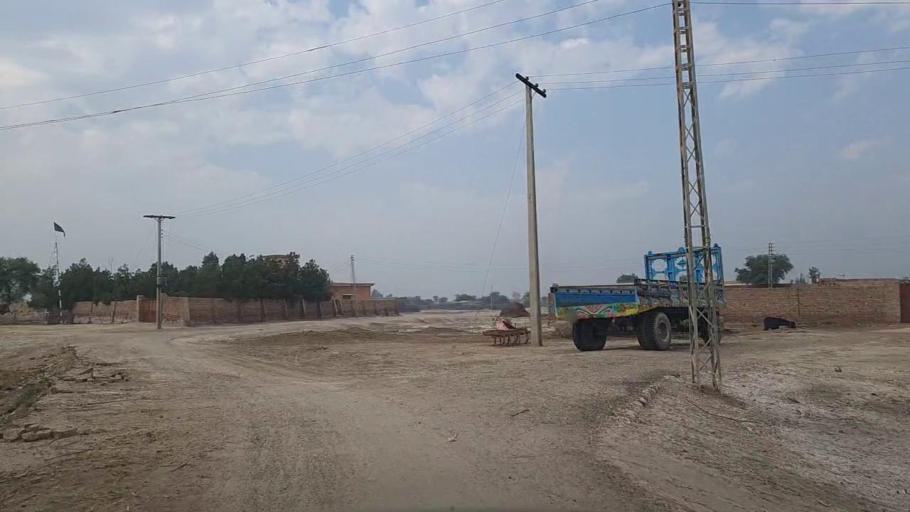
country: PK
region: Sindh
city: Nawabshah
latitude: 26.3585
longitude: 68.3996
